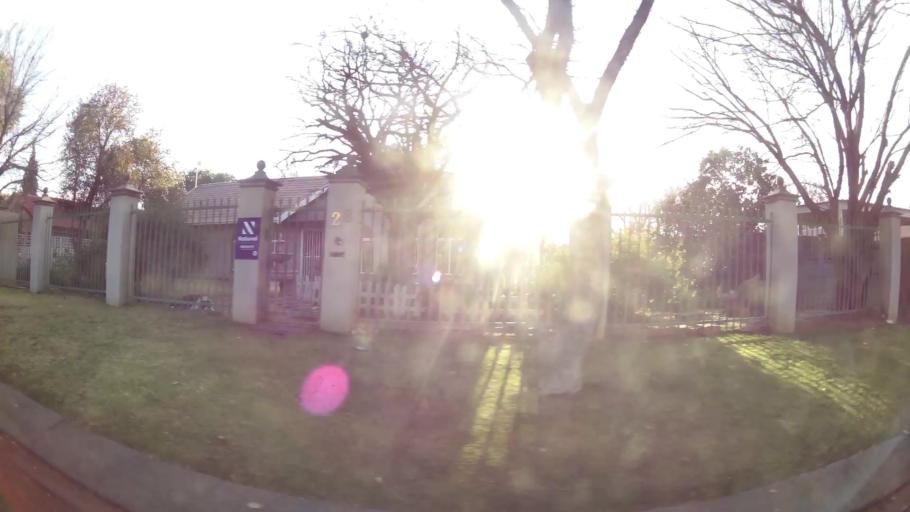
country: ZA
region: Orange Free State
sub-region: Mangaung Metropolitan Municipality
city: Bloemfontein
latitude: -29.1509
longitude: 26.1879
